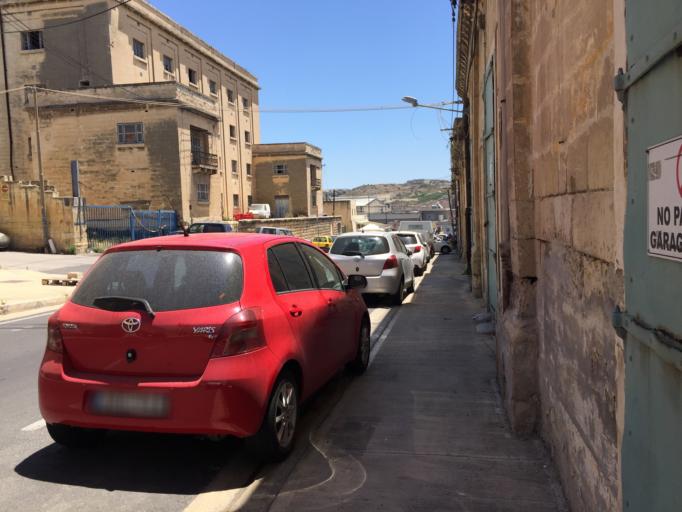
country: MT
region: Il-Marsa
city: Marsa
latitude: 35.8861
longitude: 14.4993
